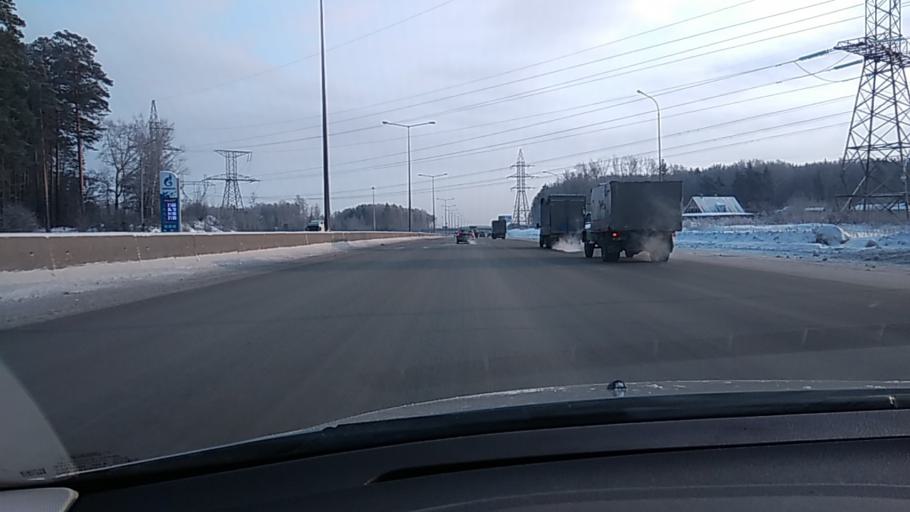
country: RU
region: Sverdlovsk
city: Istok
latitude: 56.7724
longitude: 60.7232
